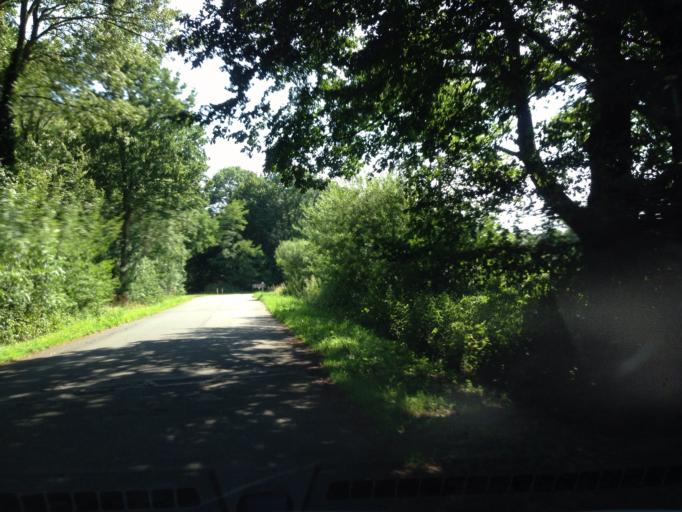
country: DE
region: North Rhine-Westphalia
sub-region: Regierungsbezirk Munster
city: Muenster
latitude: 51.9848
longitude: 7.5503
